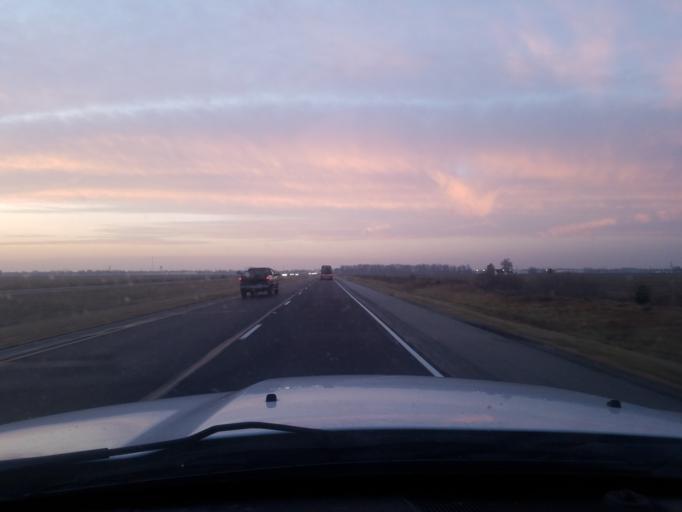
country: US
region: Indiana
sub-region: Huntington County
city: Markle
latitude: 40.8512
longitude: -85.3450
